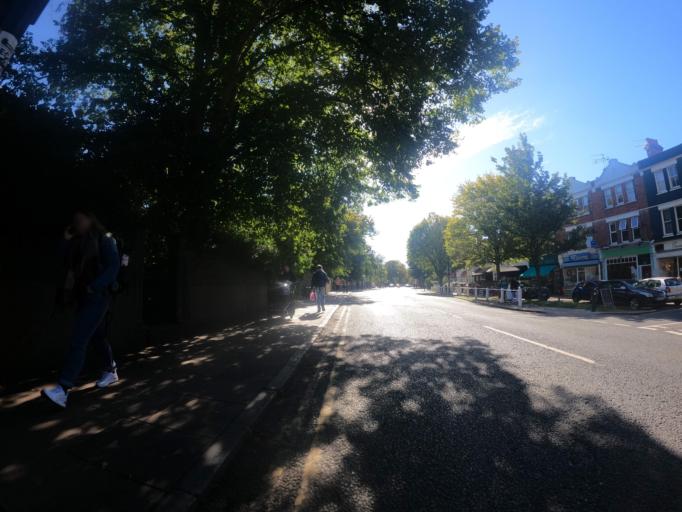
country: GB
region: England
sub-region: Greater London
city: Ealing
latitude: 51.5077
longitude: -0.3051
